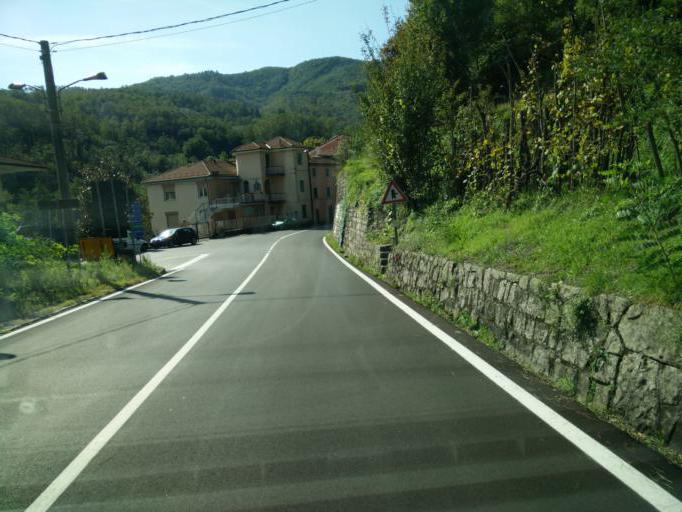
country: IT
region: Liguria
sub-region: Provincia di La Spezia
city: Carrodano
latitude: 44.2407
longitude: 9.6578
